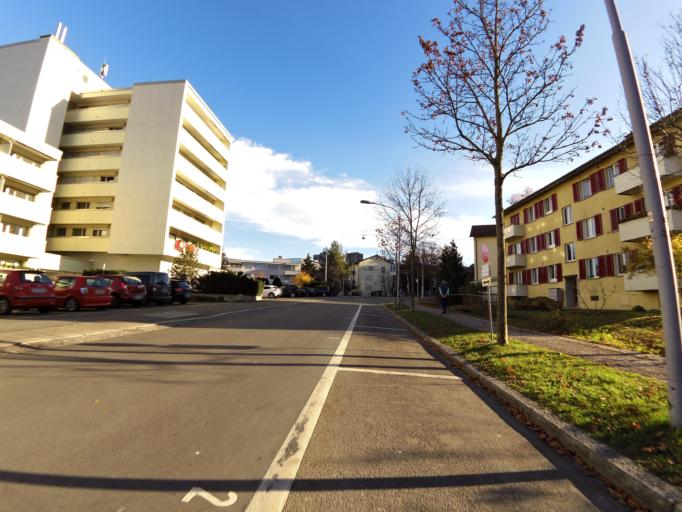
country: CH
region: Zurich
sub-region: Bezirk Zuerich
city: Zuerich (Kreis 9) / Albisrieden
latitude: 47.3706
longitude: 8.4913
